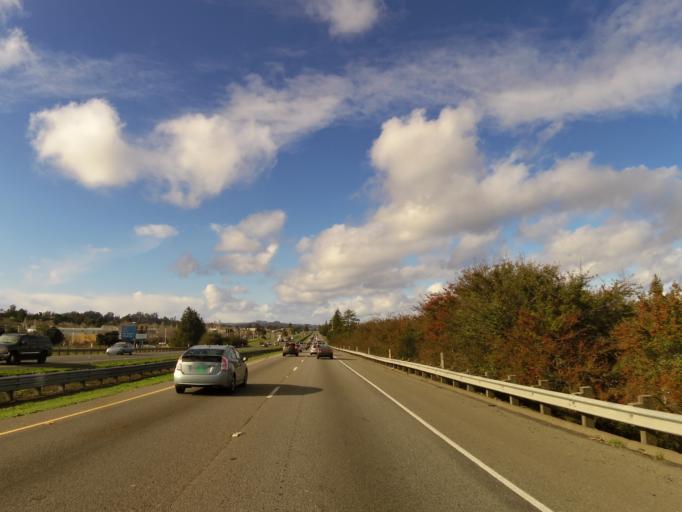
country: US
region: California
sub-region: Sonoma County
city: Petaluma
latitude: 38.2557
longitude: -122.6445
